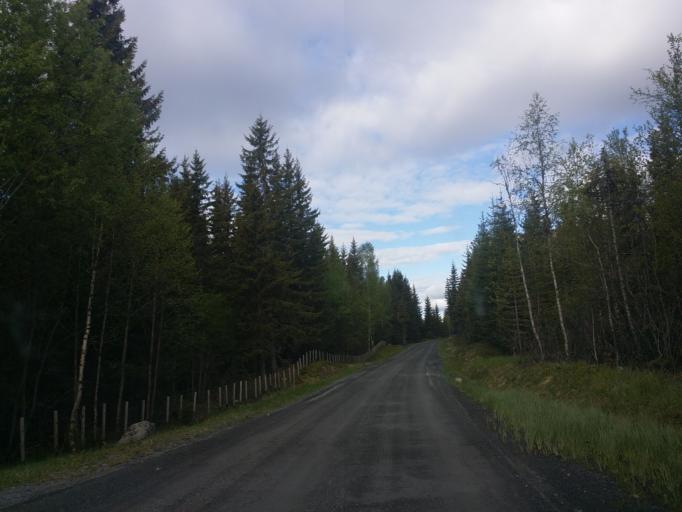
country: NO
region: Hedmark
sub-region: Ringsaker
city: Moelv
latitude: 61.0853
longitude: 10.7847
